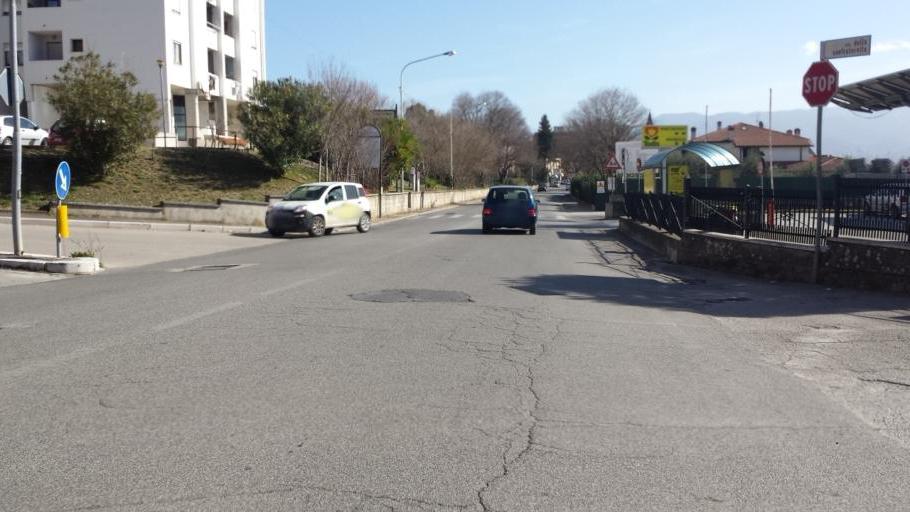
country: IT
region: Umbria
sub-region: Provincia di Terni
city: Terni
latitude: 42.5852
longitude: 12.6118
